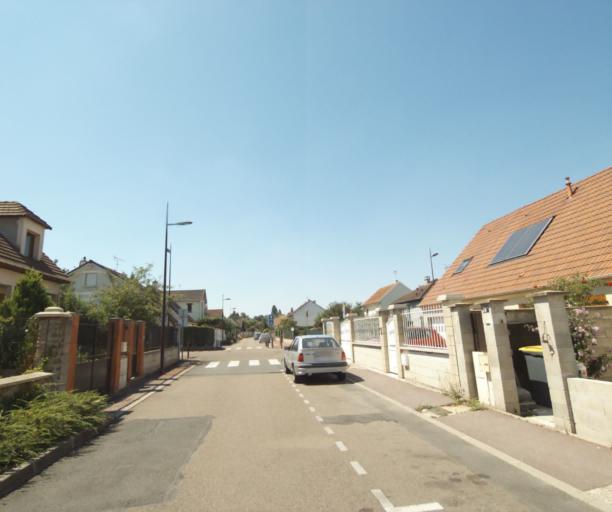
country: FR
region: Ile-de-France
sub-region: Departement de Seine-et-Marne
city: Thorigny-sur-Marne
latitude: 48.8768
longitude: 2.7272
